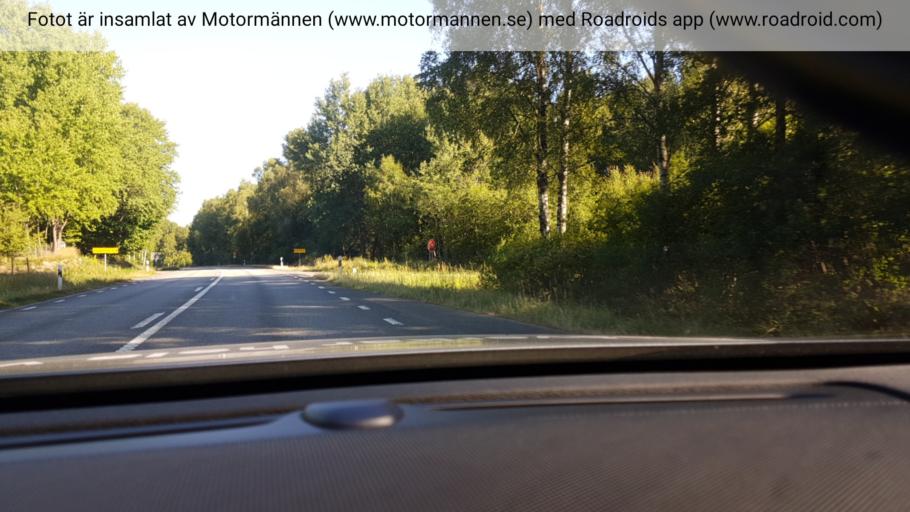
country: SE
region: Kronoberg
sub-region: Markaryds Kommun
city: Markaryd
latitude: 56.4350
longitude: 13.6155
